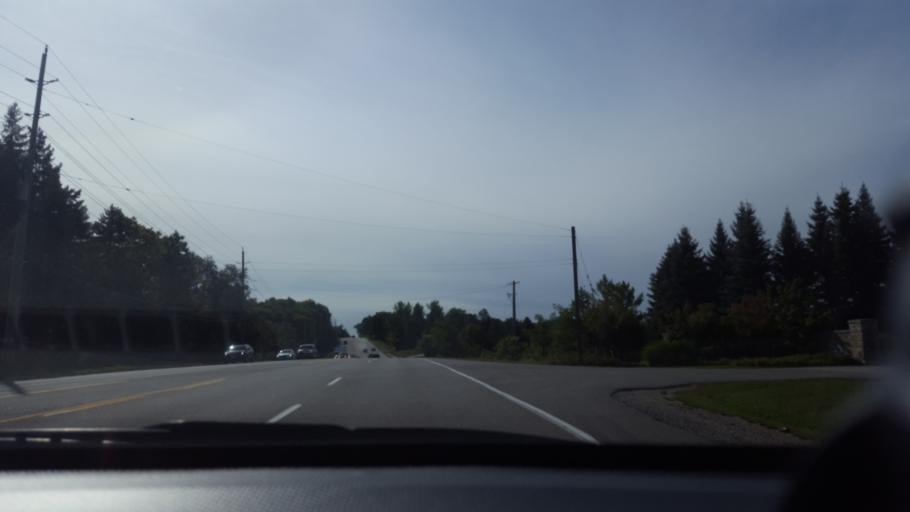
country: CA
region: Ontario
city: Newmarket
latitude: 43.9822
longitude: -79.4917
